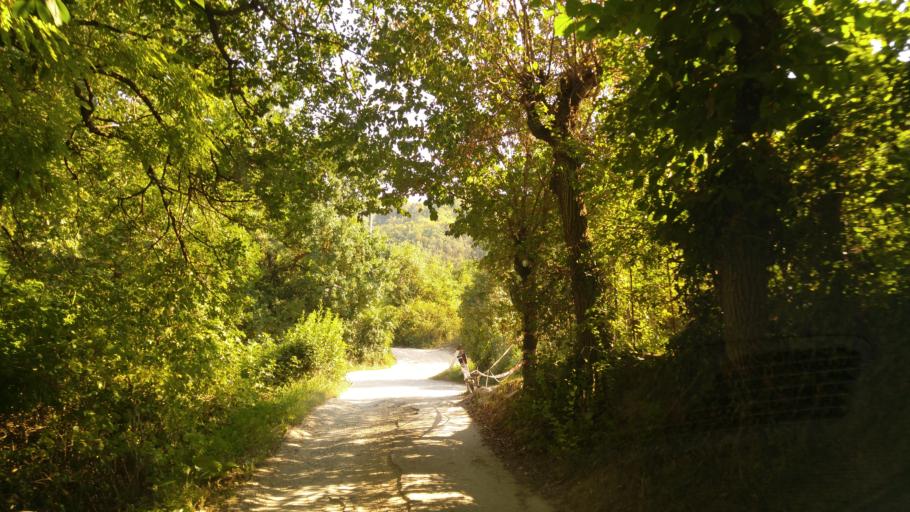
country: IT
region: The Marches
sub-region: Provincia di Pesaro e Urbino
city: Fossombrone
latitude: 43.6781
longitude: 12.7923
